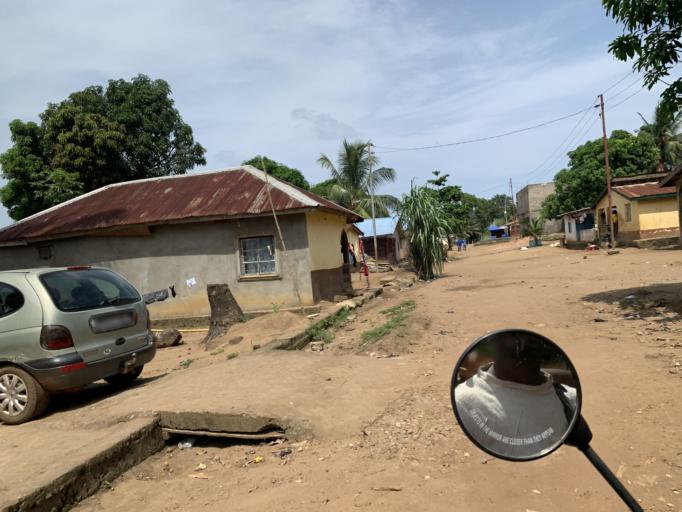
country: SL
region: Western Area
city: Hastings
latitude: 8.4083
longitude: -13.1351
